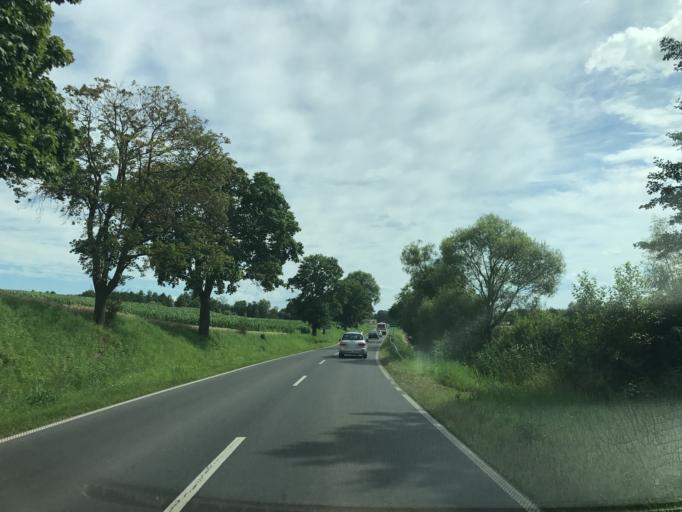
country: PL
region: Kujawsko-Pomorskie
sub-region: Powiat rypinski
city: Rypin
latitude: 53.1314
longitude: 19.3849
